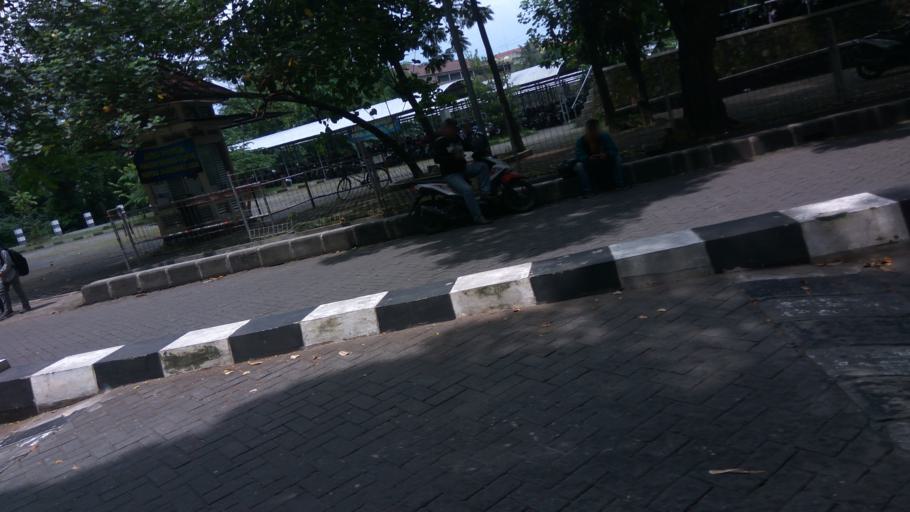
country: ID
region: Daerah Istimewa Yogyakarta
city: Yogyakarta
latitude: -7.7670
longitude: 110.3833
